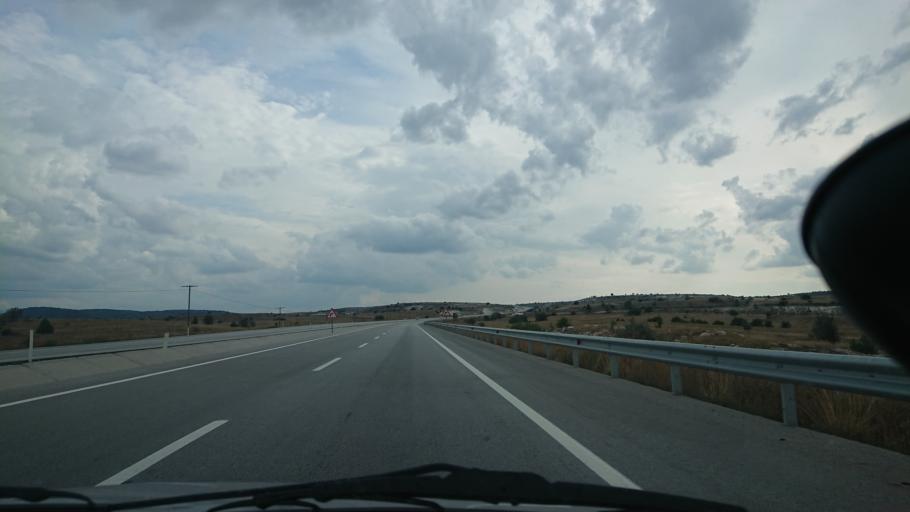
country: TR
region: Kuetahya
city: Cavdarhisar
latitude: 39.1651
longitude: 29.5936
